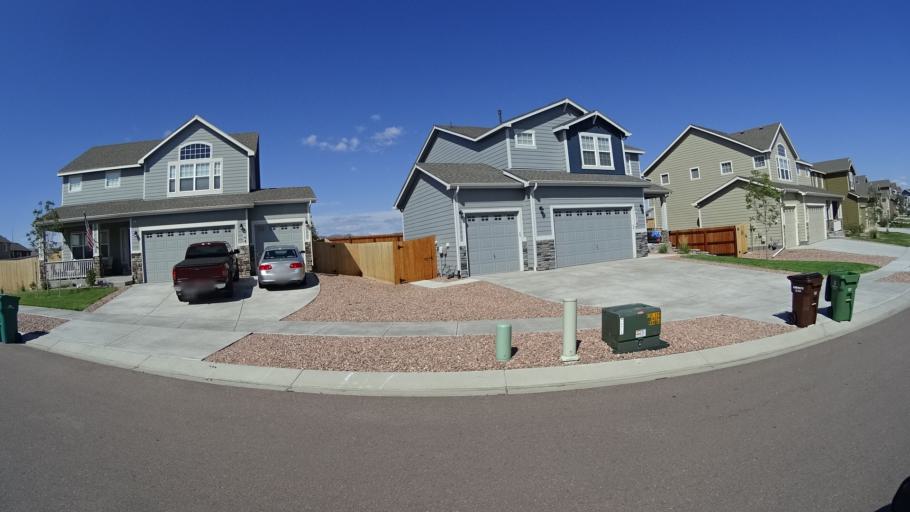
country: US
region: Colorado
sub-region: El Paso County
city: Cimarron Hills
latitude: 38.9301
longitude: -104.7098
